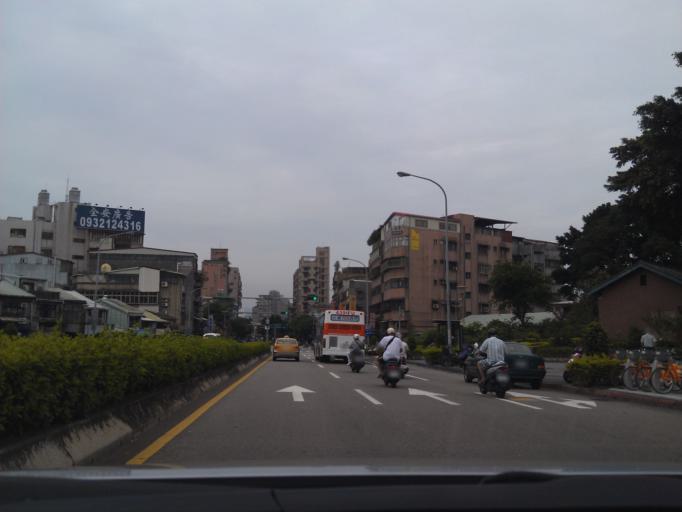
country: TW
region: Taipei
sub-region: Taipei
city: Banqiao
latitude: 25.0328
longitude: 121.4978
